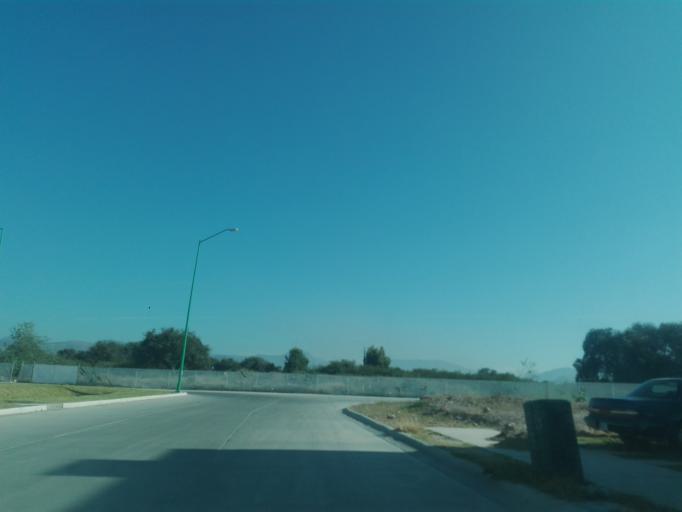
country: MX
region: Guanajuato
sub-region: Leon
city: Ladrilleras del Refugio
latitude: 21.0700
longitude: -101.5575
